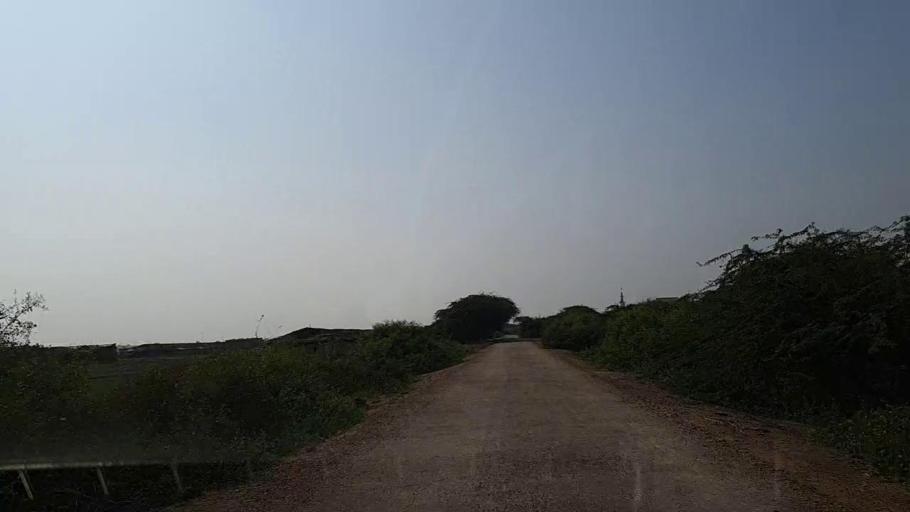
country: PK
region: Sindh
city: Mirpur Sakro
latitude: 24.6408
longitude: 67.6678
